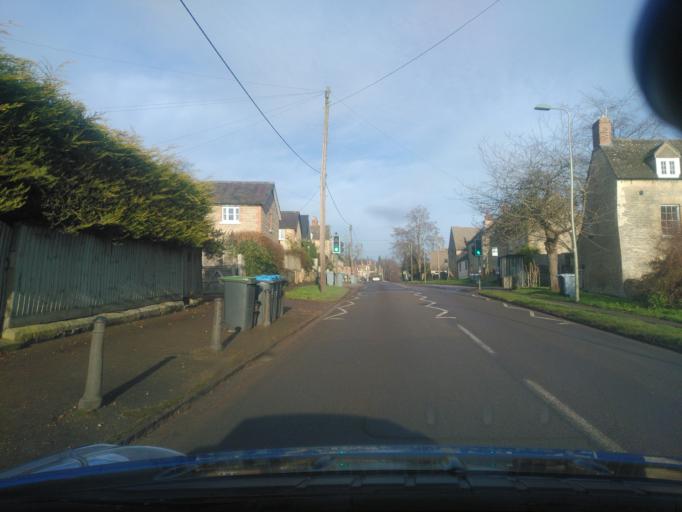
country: GB
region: England
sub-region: Oxfordshire
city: Woodstock
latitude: 51.8519
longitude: -1.3609
